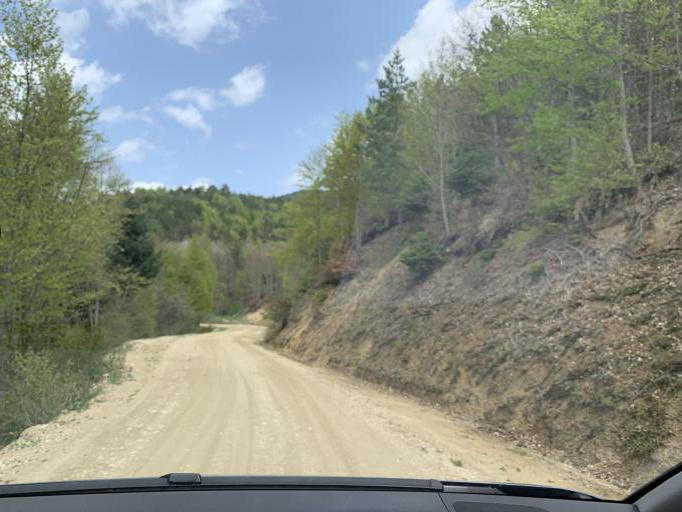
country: TR
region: Bolu
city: Bolu
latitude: 40.8332
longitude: 31.6719
